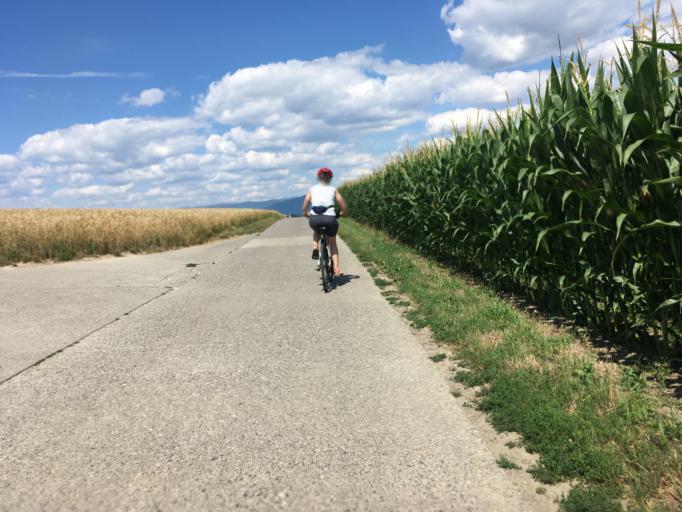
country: CH
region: Fribourg
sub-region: See District
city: Bas-Vully
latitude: 46.9698
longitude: 7.1021
